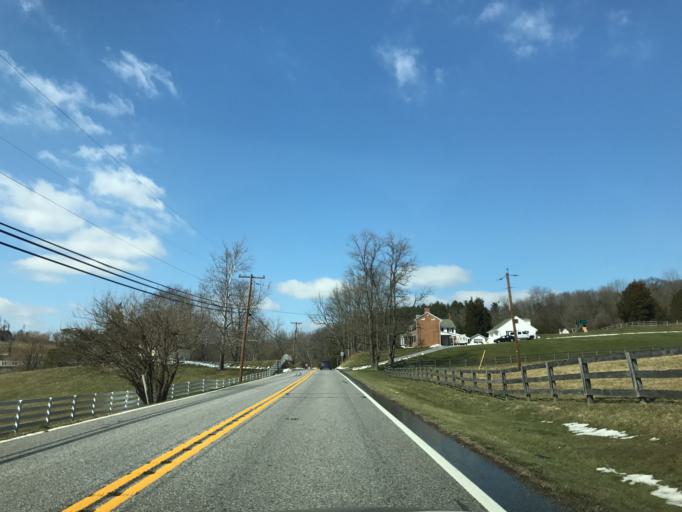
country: US
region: Maryland
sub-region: Baltimore County
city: Hunt Valley
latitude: 39.5518
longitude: -76.7436
